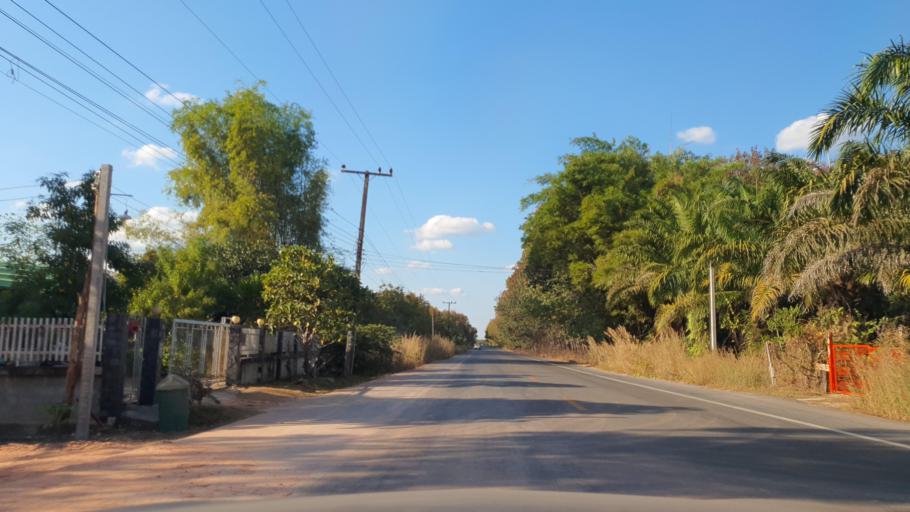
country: TH
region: Nong Khai
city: Bueng Khong Long
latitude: 18.0158
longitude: 104.0010
